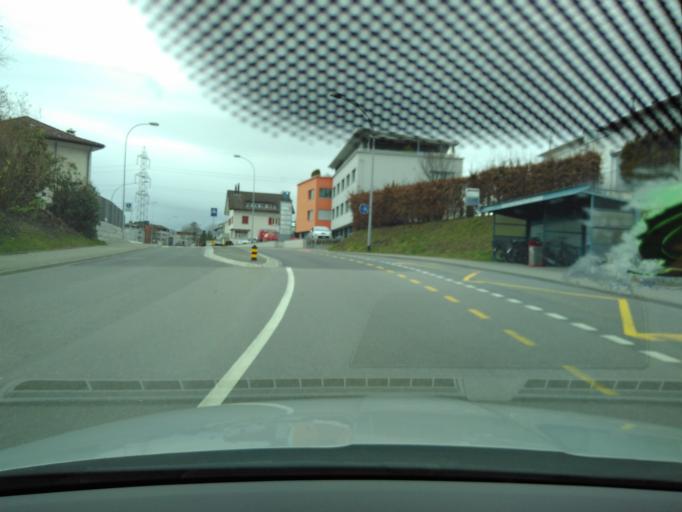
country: CH
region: Lucerne
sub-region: Hochdorf District
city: Emmen
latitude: 47.0975
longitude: 8.2714
